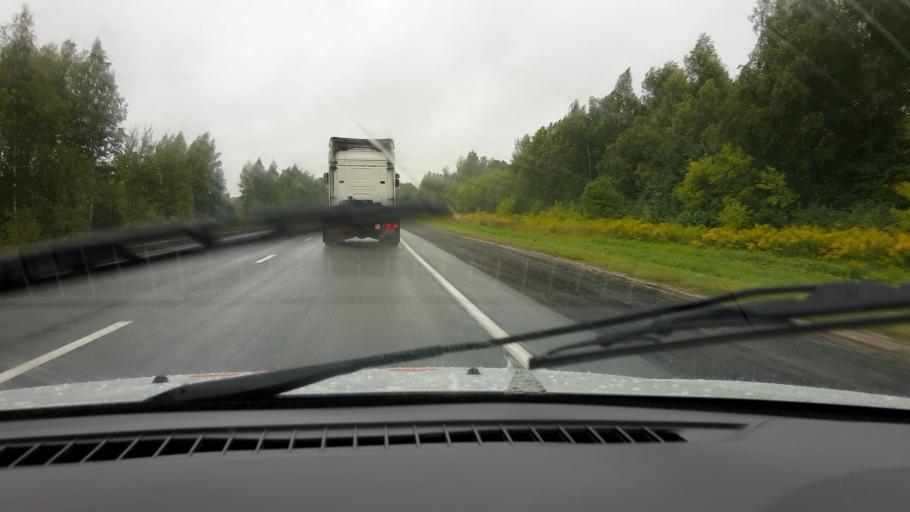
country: RU
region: Nizjnij Novgorod
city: Spasskoye
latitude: 56.0437
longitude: 45.5999
